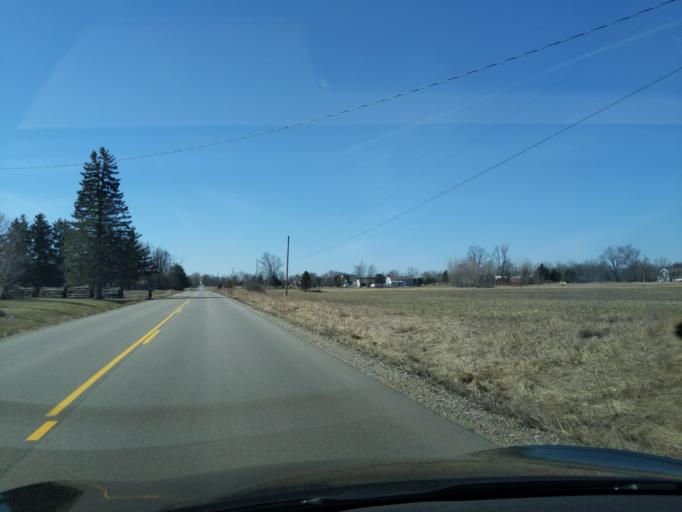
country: US
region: Michigan
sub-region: Eaton County
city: Grand Ledge
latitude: 42.7265
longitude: -84.8050
